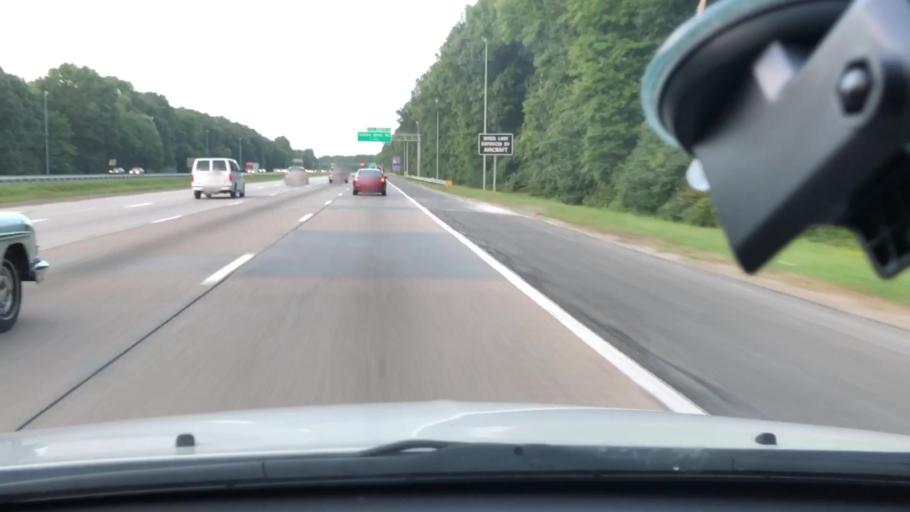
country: US
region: Virginia
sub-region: City of Chesapeake
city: Chesapeake
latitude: 36.7944
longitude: -76.2120
